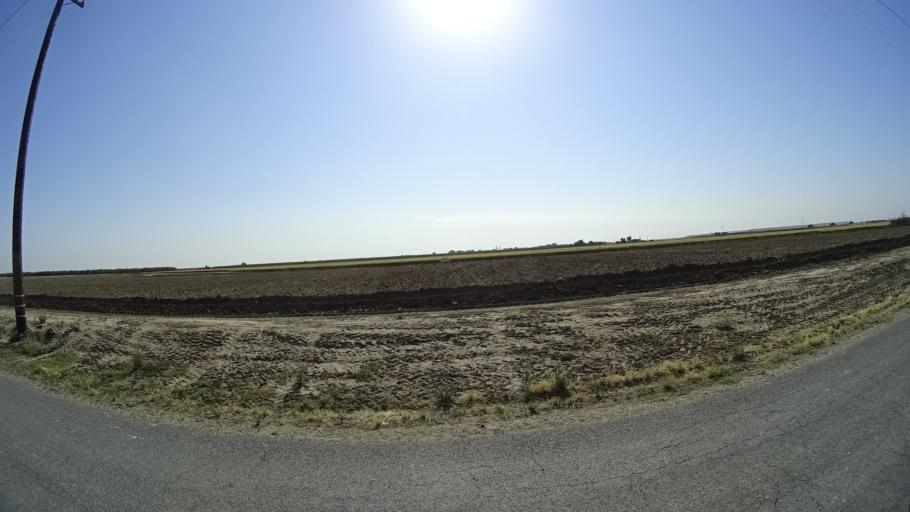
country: US
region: California
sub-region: Kings County
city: Home Garden
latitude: 36.2577
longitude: -119.5831
